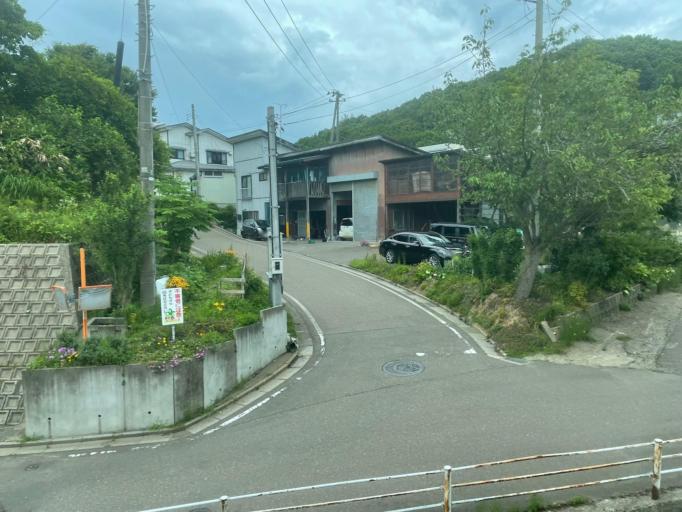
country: JP
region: Niigata
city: Joetsu
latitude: 37.1599
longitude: 138.2208
